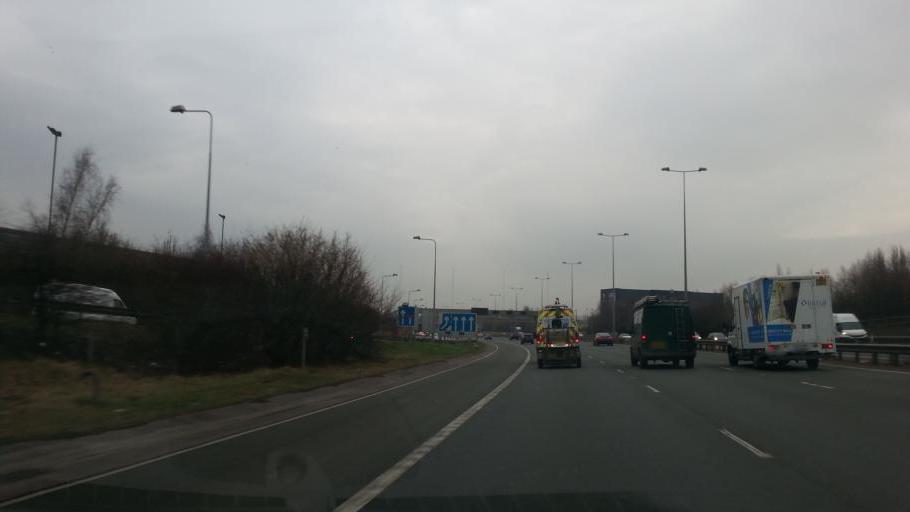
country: GB
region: England
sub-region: Borough of Tameside
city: Ashton-under-Lyne
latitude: 53.4828
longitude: -2.1157
